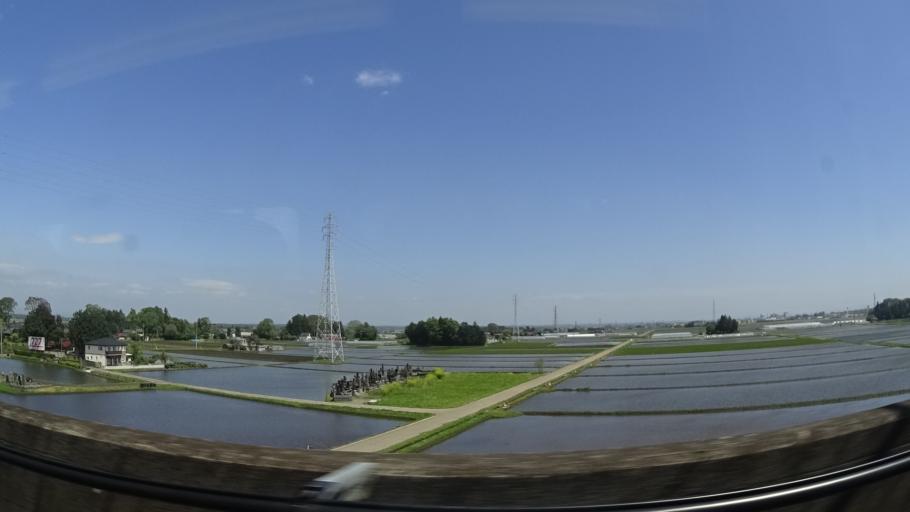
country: JP
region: Tochigi
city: Ujiie
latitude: 36.7153
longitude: 139.9248
